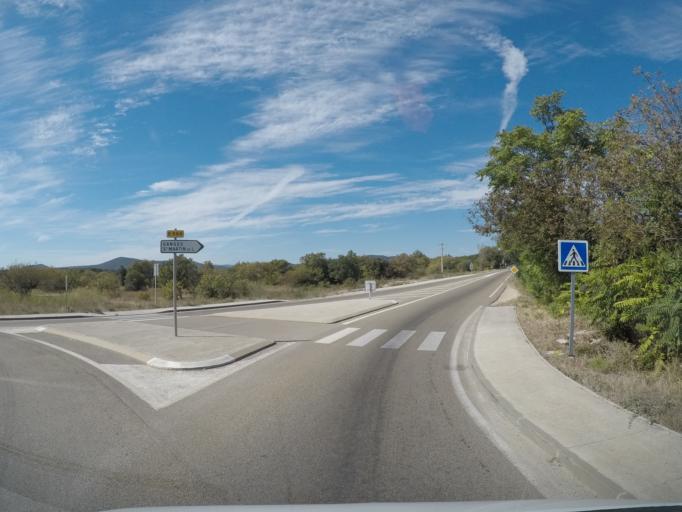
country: FR
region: Languedoc-Roussillon
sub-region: Departement de l'Herault
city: Saint-Martin-de-Londres
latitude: 43.7581
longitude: 3.7511
